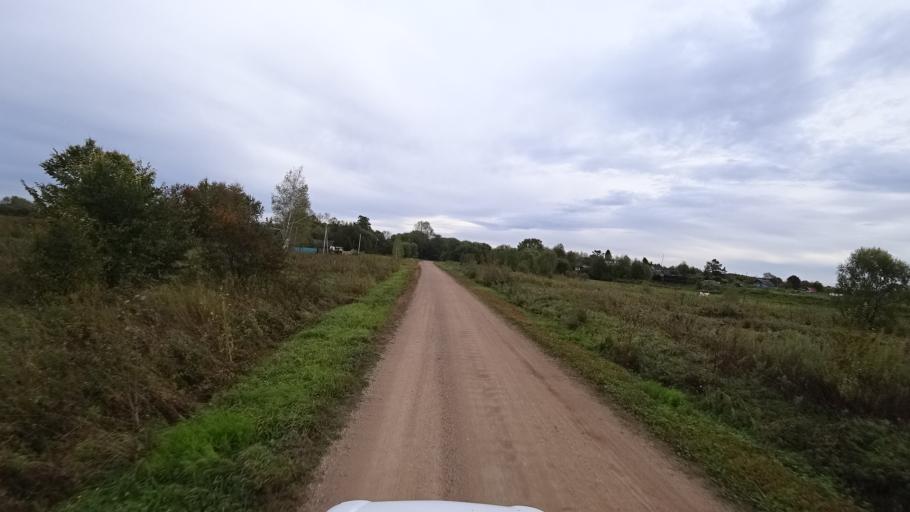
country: RU
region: Amur
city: Arkhara
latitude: 49.4361
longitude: 130.2642
